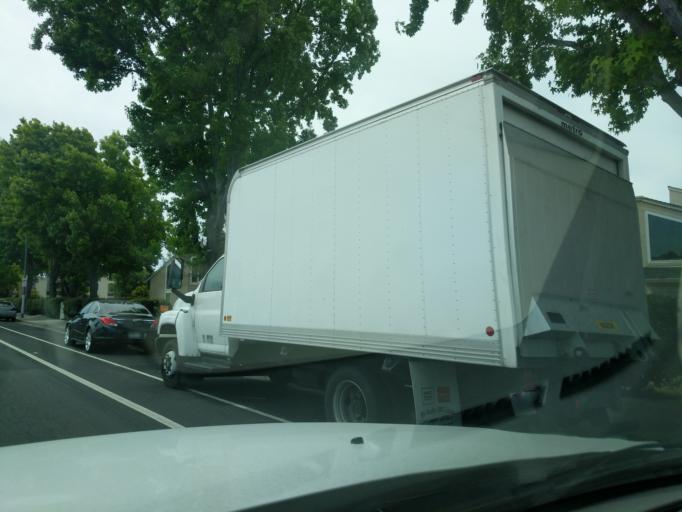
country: US
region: California
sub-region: Alameda County
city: Hayward
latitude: 37.6389
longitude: -122.0640
